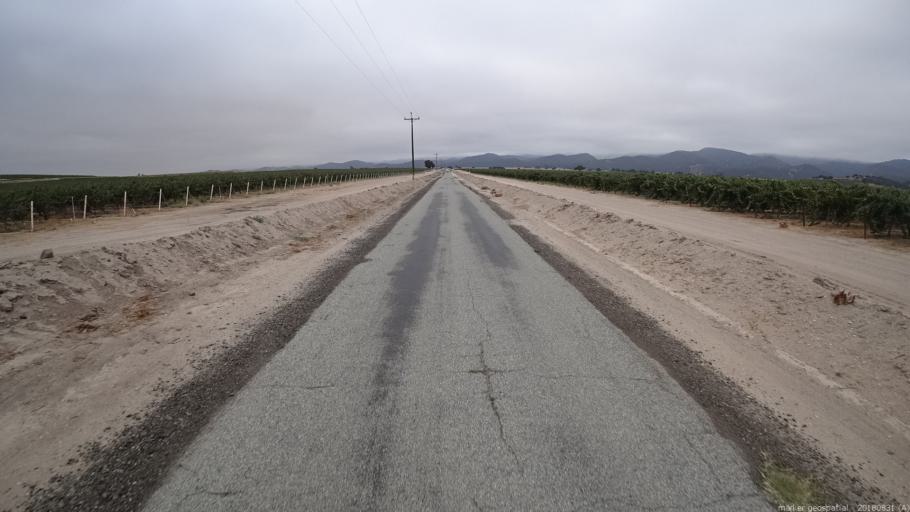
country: US
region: California
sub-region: Monterey County
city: King City
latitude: 36.1206
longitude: -121.0874
